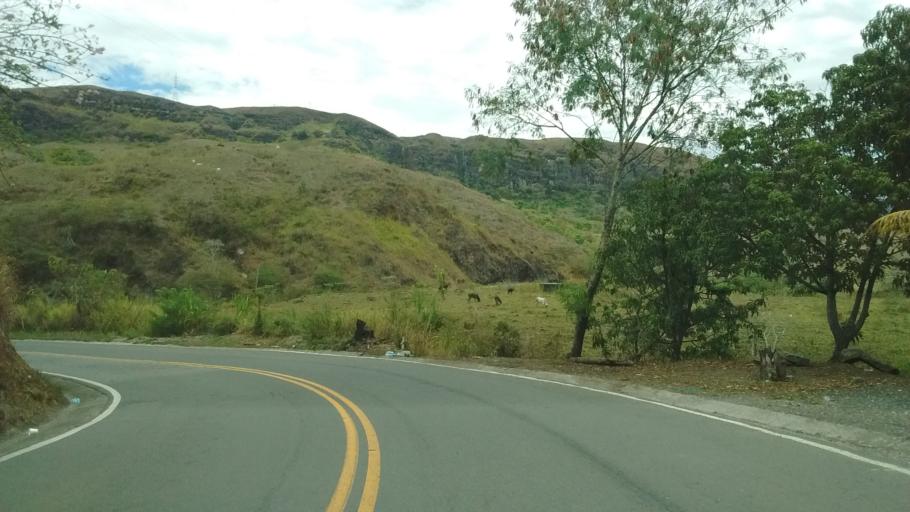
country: CO
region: Cauca
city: La Sierra
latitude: 2.2041
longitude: -76.8123
